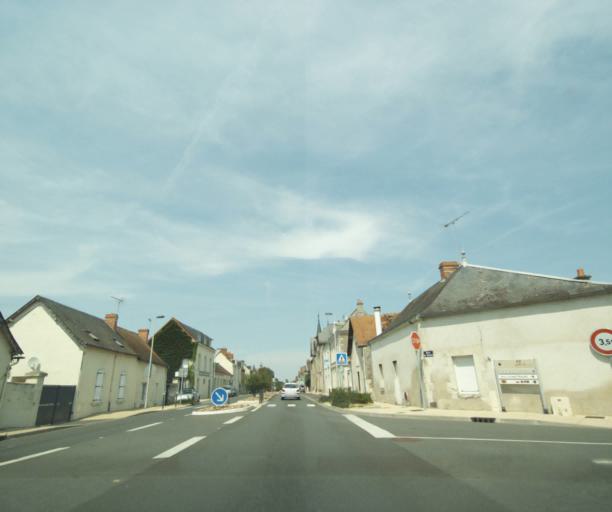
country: FR
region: Poitou-Charentes
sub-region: Departement de la Vienne
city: Antran
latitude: 46.8730
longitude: 0.5632
